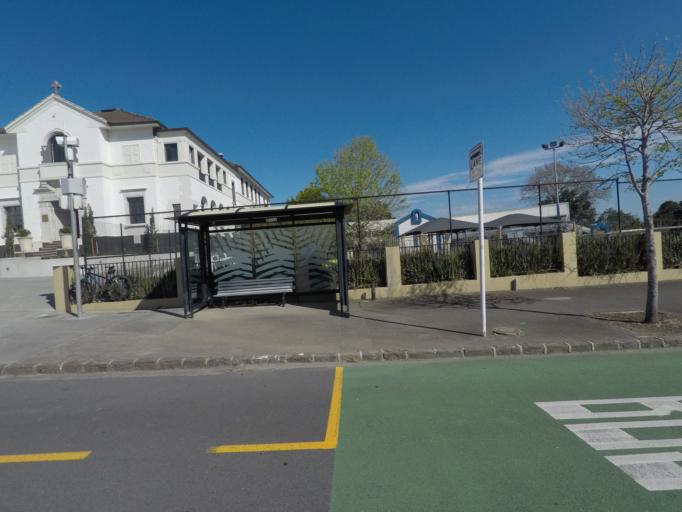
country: NZ
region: Auckland
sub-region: Auckland
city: Auckland
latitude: -36.8670
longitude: 174.7399
